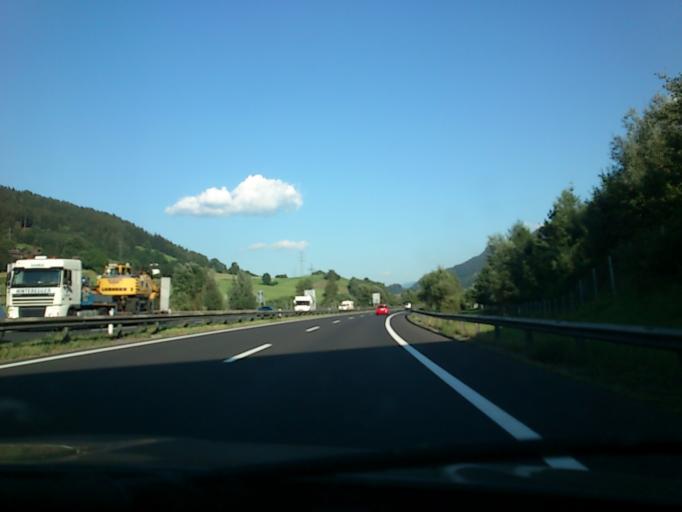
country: AT
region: Styria
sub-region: Politischer Bezirk Liezen
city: Selzthal
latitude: 47.5323
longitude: 14.3191
